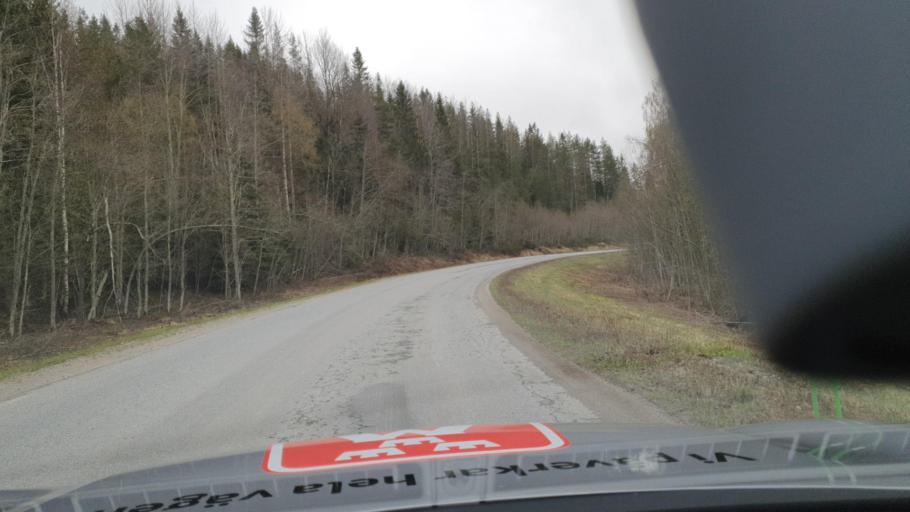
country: SE
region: Vaesternorrland
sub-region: OErnskoeldsviks Kommun
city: Husum
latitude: 63.5689
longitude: 19.0437
